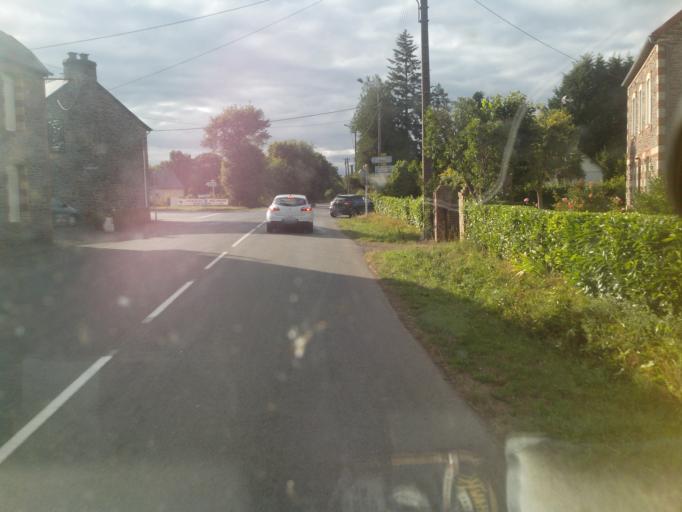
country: FR
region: Brittany
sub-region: Departement d'Ille-et-Vilaine
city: Paimpont
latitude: 48.0659
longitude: -2.1889
